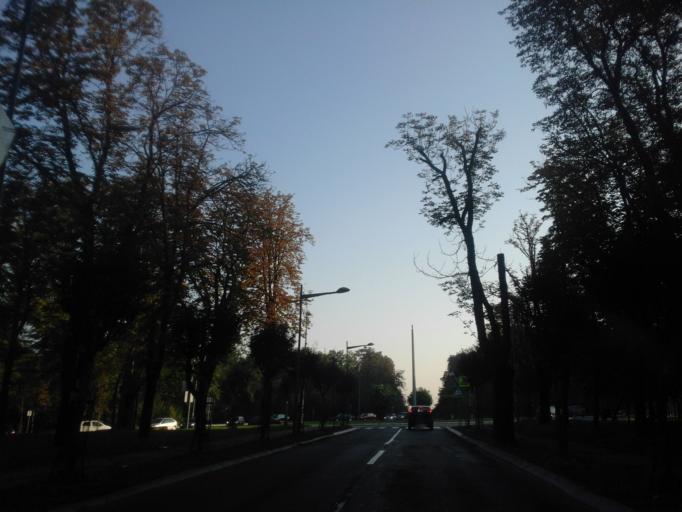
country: RS
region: Central Serbia
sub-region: Belgrade
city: Savski Venac
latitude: 44.7883
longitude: 20.4435
